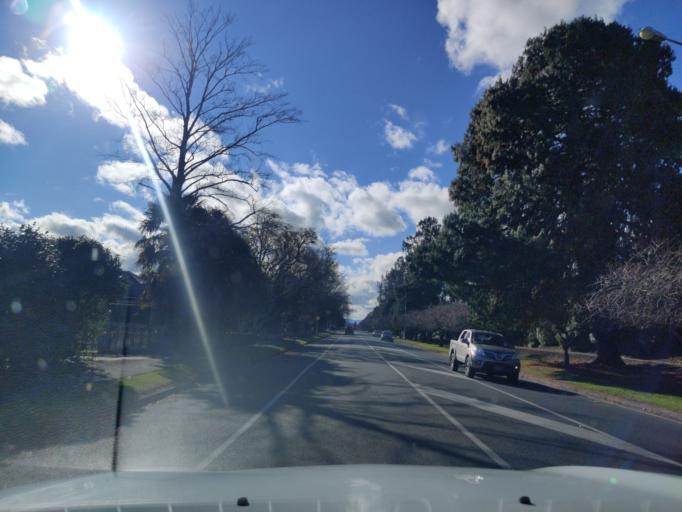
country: NZ
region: Waikato
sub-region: Matamata-Piako District
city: Matamata
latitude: -37.8202
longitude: 175.7711
